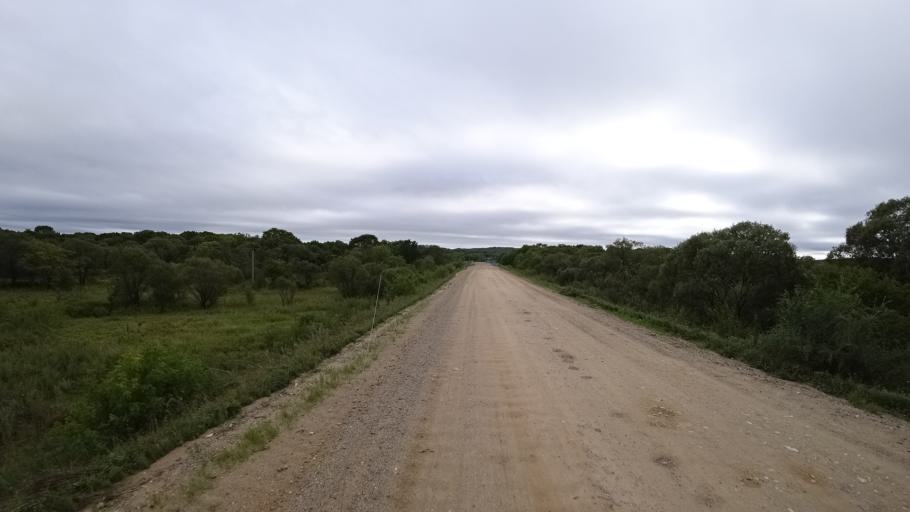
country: RU
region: Primorskiy
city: Rettikhovka
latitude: 44.1284
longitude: 132.6417
